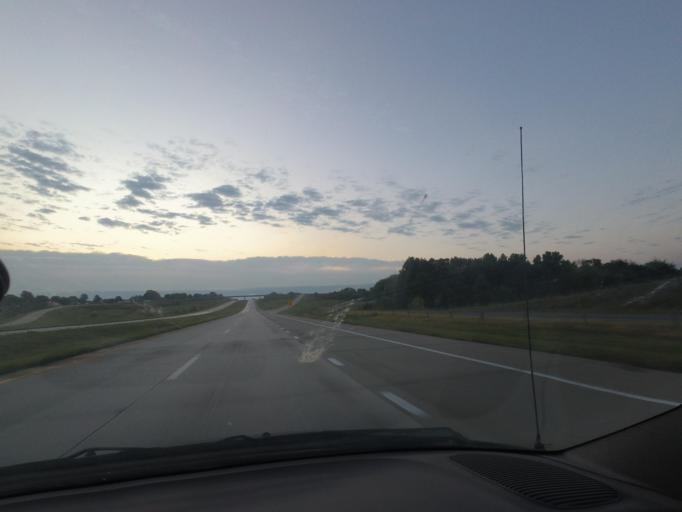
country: US
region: Missouri
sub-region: Macon County
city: Macon
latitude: 39.7563
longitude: -92.6322
